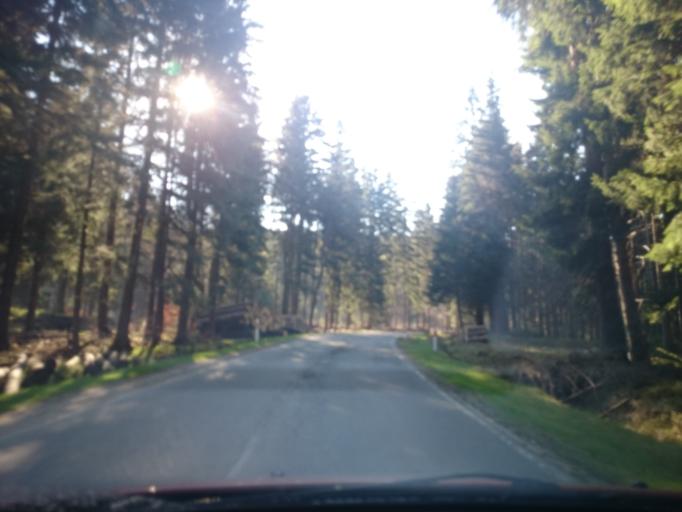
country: PL
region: Lower Silesian Voivodeship
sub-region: Powiat klodzki
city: Duszniki-Zdroj
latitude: 50.3247
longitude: 16.4134
